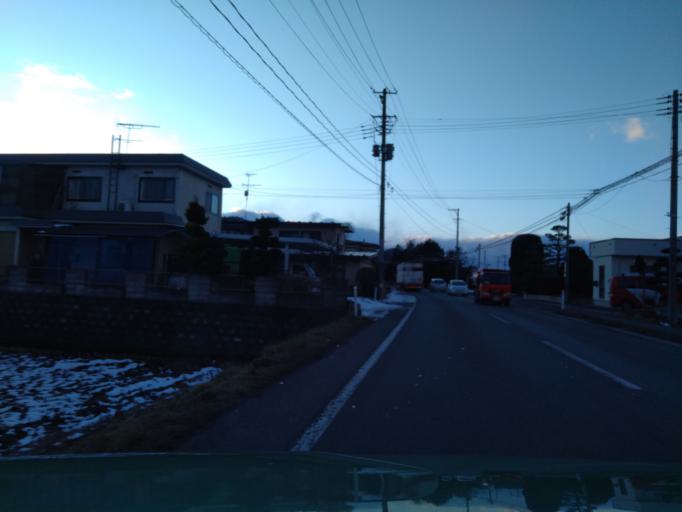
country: JP
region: Iwate
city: Shizukuishi
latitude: 39.6908
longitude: 141.0678
